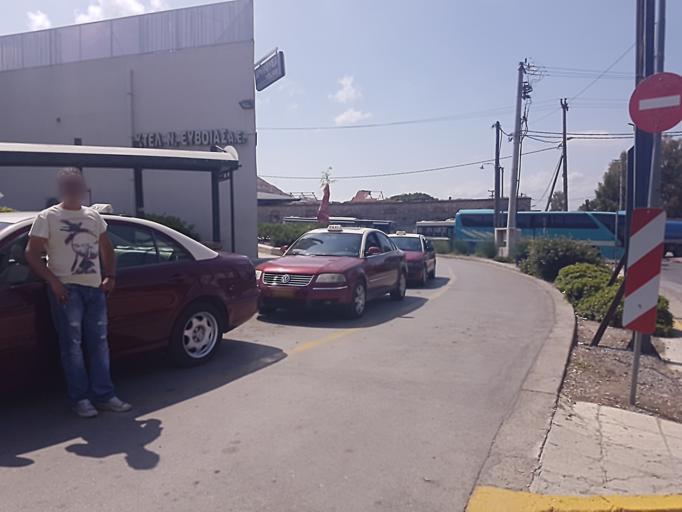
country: GR
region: Central Greece
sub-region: Nomos Evvoias
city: Chalkida
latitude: 38.4574
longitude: 23.6115
